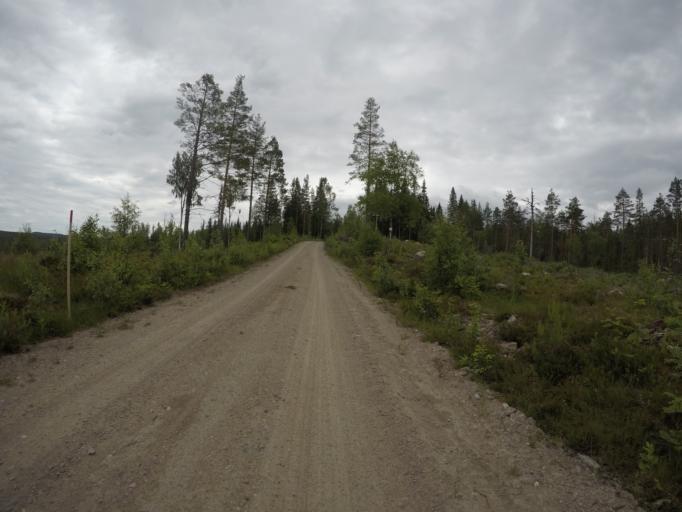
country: SE
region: Dalarna
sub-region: Ludvika Kommun
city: Abborrberget
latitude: 60.0833
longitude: 14.5543
